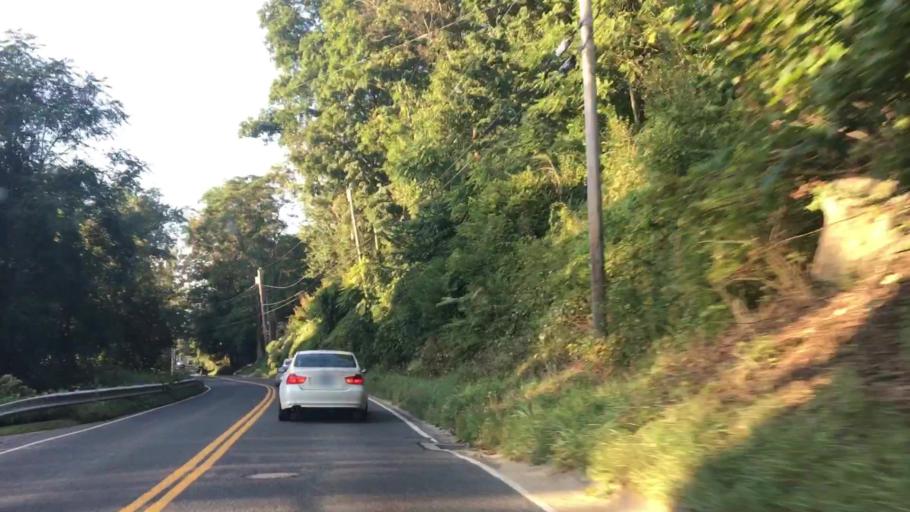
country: US
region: Connecticut
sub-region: Litchfield County
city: New Milford
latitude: 41.5628
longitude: -73.4043
